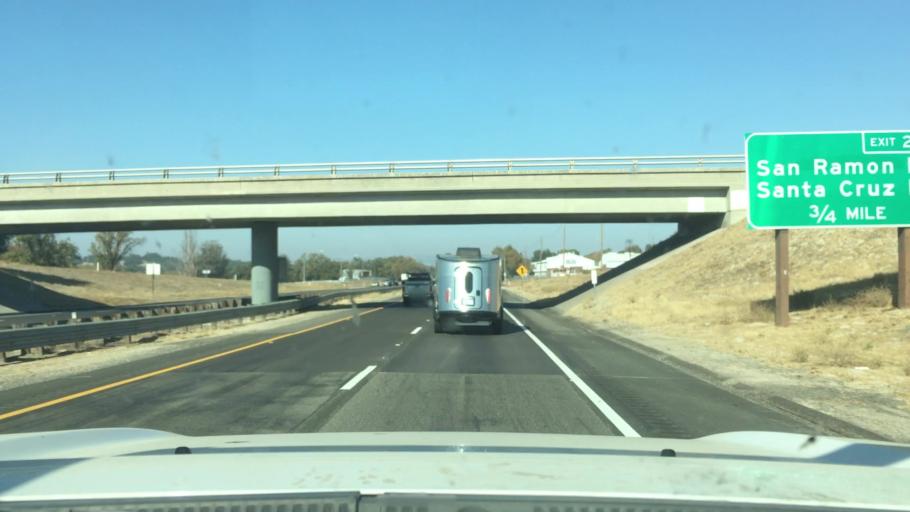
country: US
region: California
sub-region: San Luis Obispo County
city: Atascadero
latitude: 35.5131
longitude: -120.6992
